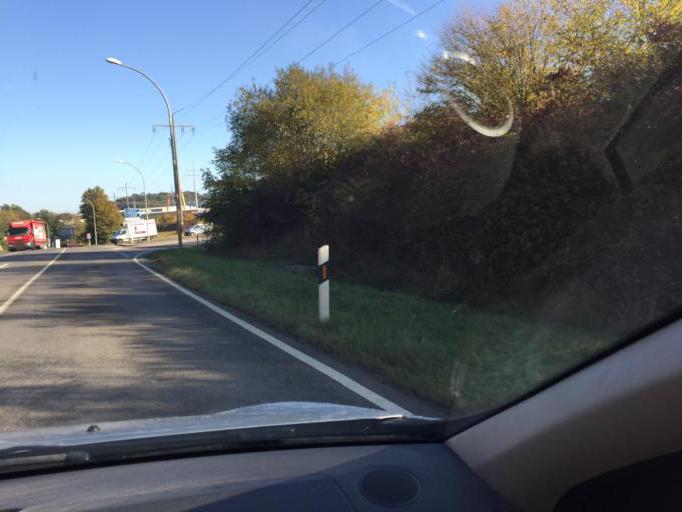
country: LU
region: Luxembourg
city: Colmar
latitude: 49.8003
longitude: 6.0994
